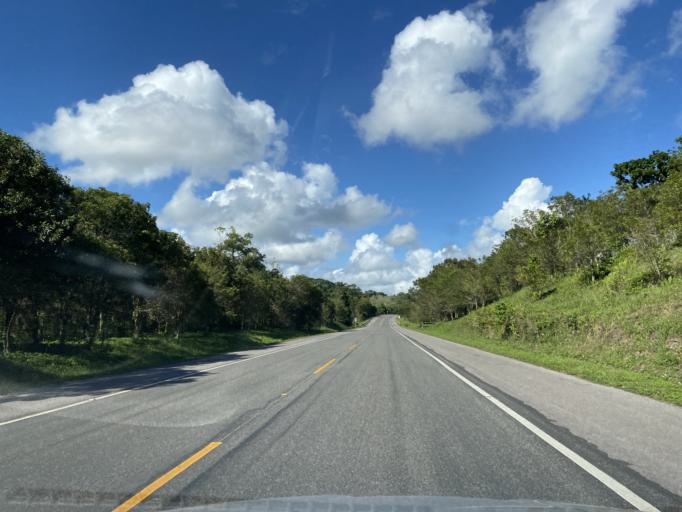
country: DO
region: Monte Plata
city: Majagual
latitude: 19.0295
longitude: -69.8249
